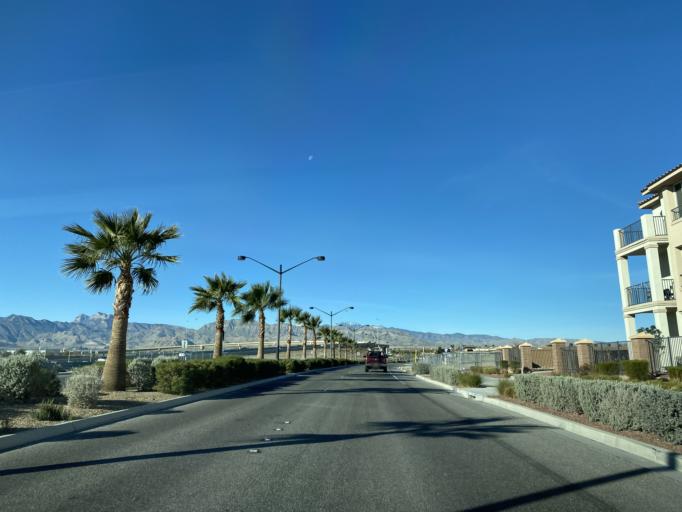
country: US
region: Nevada
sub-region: Clark County
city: Las Vegas
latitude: 36.2772
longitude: -115.2557
